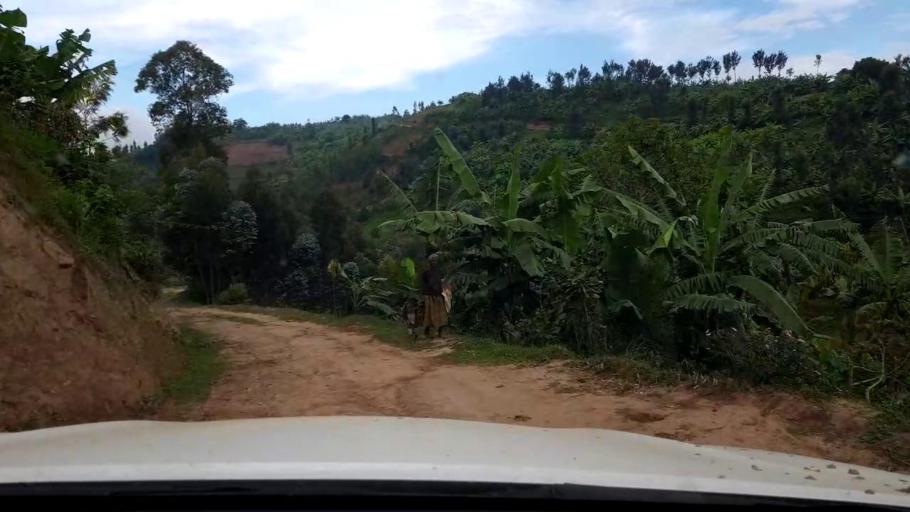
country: RW
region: Western Province
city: Kibuye
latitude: -2.0006
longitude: 29.3697
